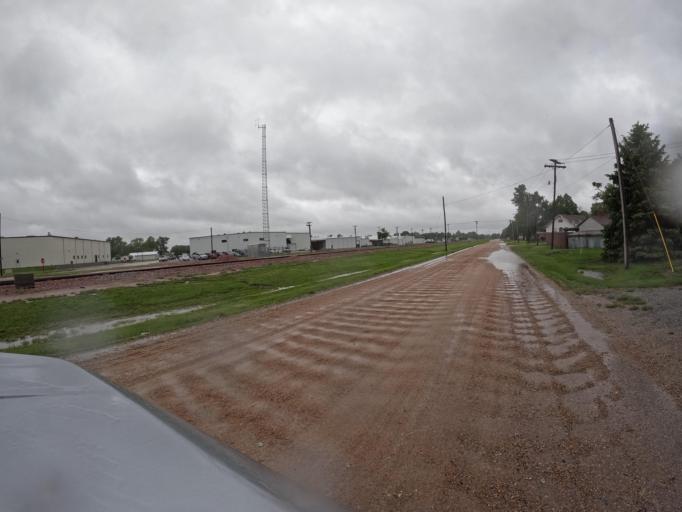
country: US
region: Nebraska
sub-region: Saline County
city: Wilber
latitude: 40.3927
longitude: -96.9151
